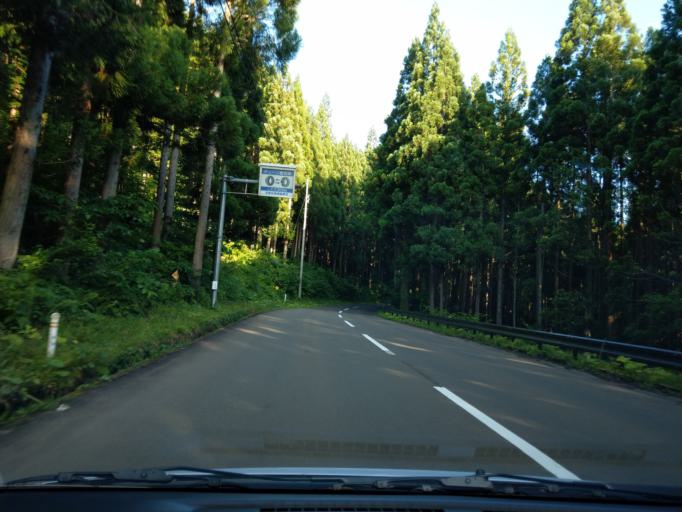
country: JP
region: Akita
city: Kakunodatemachi
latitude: 39.8936
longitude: 140.4632
